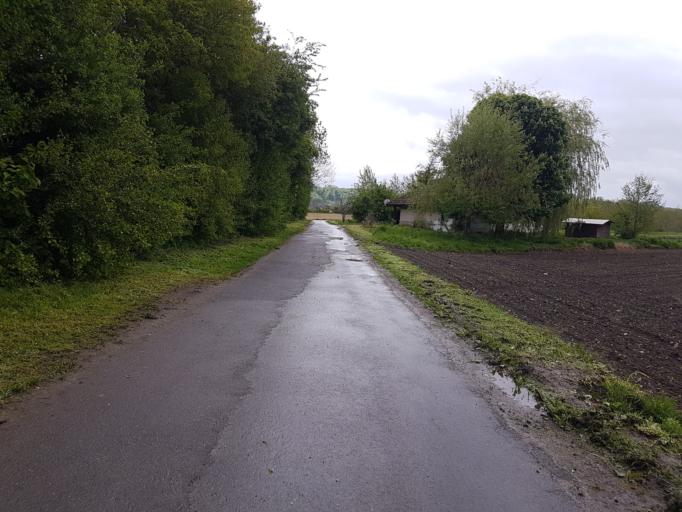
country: CH
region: Vaud
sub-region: Jura-Nord vaudois District
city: Yverdon-les-Bains
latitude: 46.7652
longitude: 6.6221
